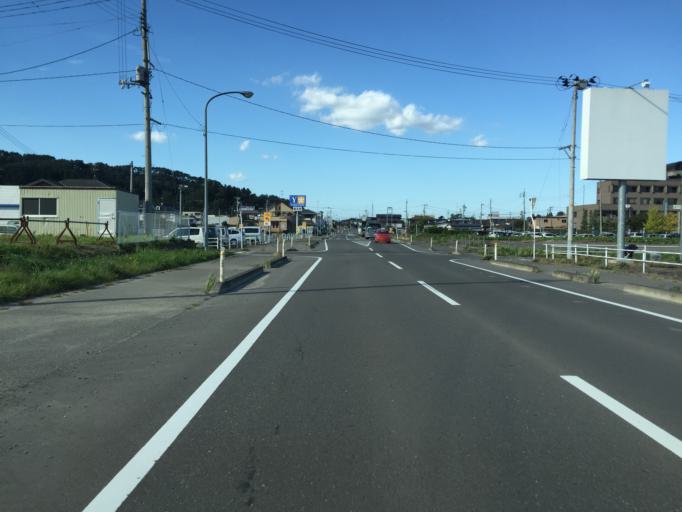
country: JP
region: Miyagi
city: Marumori
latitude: 37.9095
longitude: 140.7641
